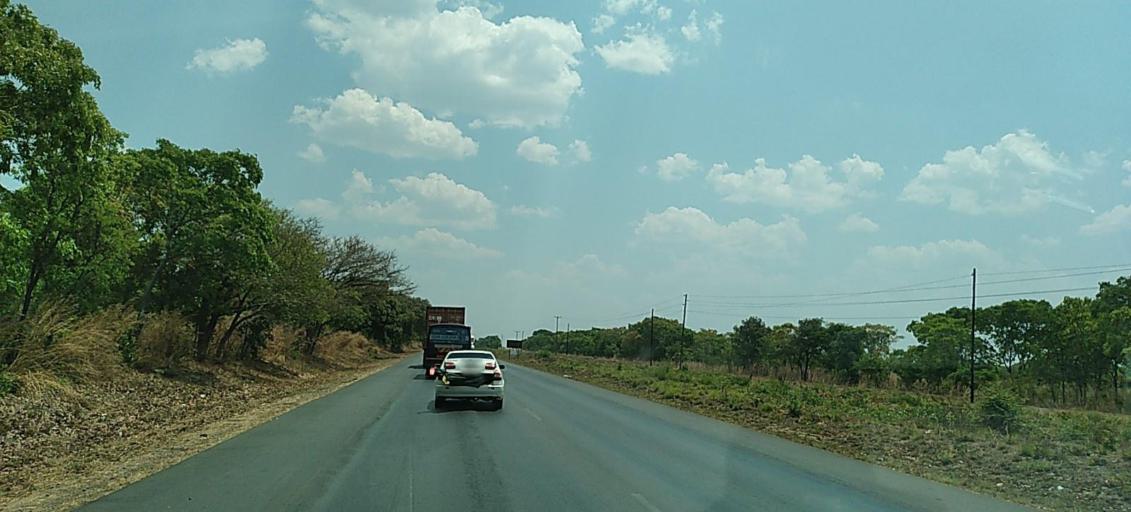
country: ZM
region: Central
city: Kabwe
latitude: -14.3329
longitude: 28.5350
